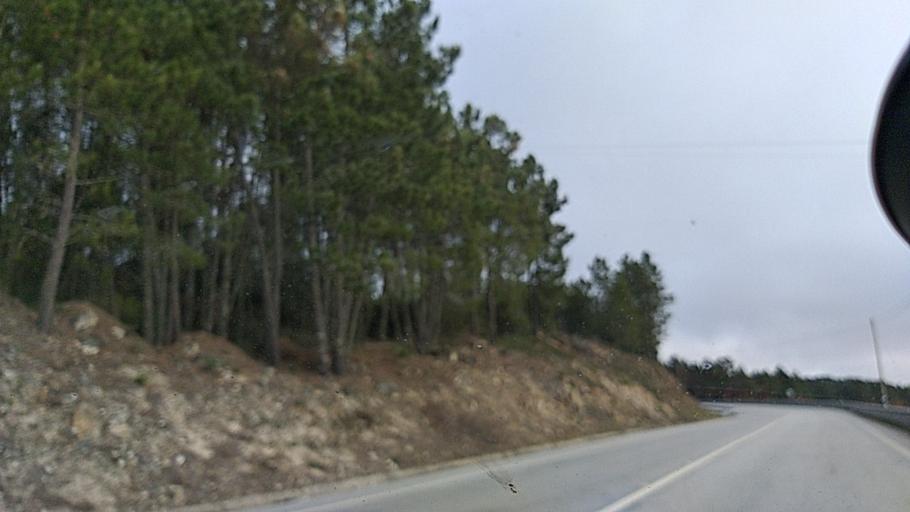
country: PT
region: Guarda
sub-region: Aguiar da Beira
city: Aguiar da Beira
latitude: 40.7838
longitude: -7.5030
